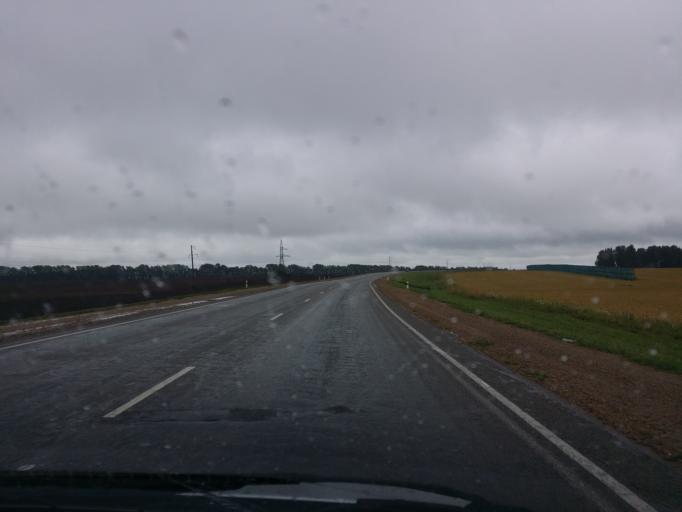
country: RU
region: Altai Krai
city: Nalobikha
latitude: 53.2453
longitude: 84.5864
